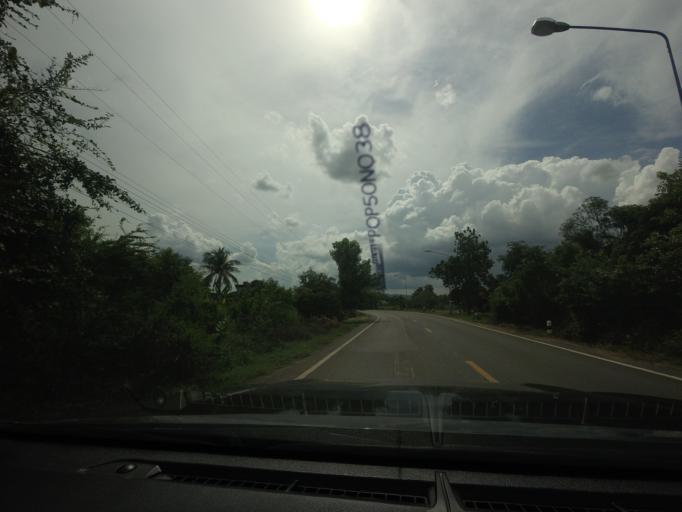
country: TH
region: Kanchanaburi
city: Bo Phloi
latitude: 14.1675
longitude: 99.4370
